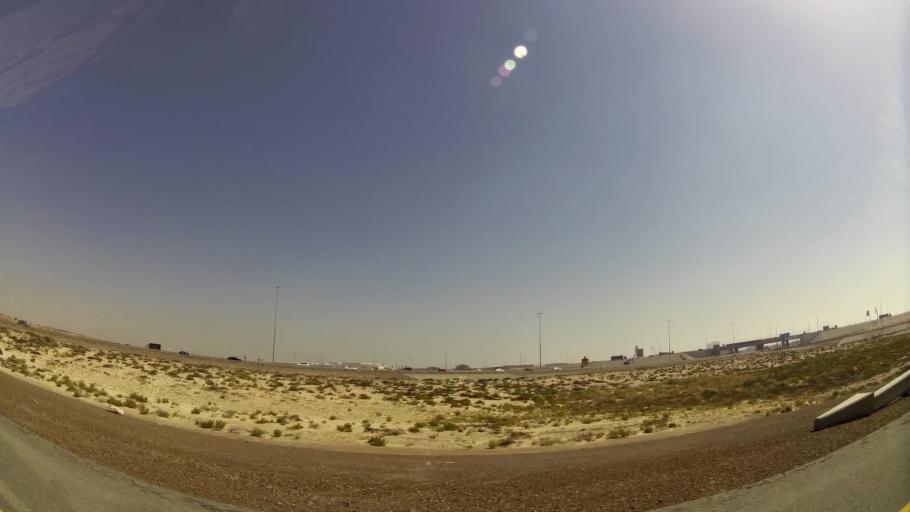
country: AE
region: Dubai
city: Dubai
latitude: 24.9444
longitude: 55.0592
